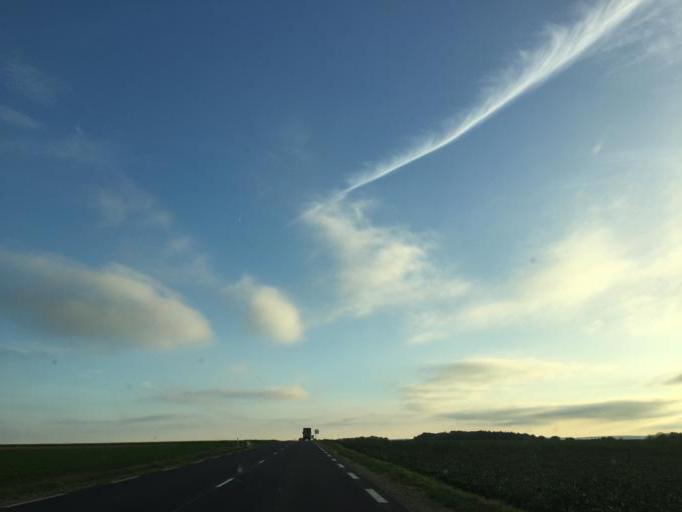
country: FR
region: Bourgogne
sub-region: Departement de l'Yonne
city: Sergines
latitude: 48.3520
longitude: 3.2319
